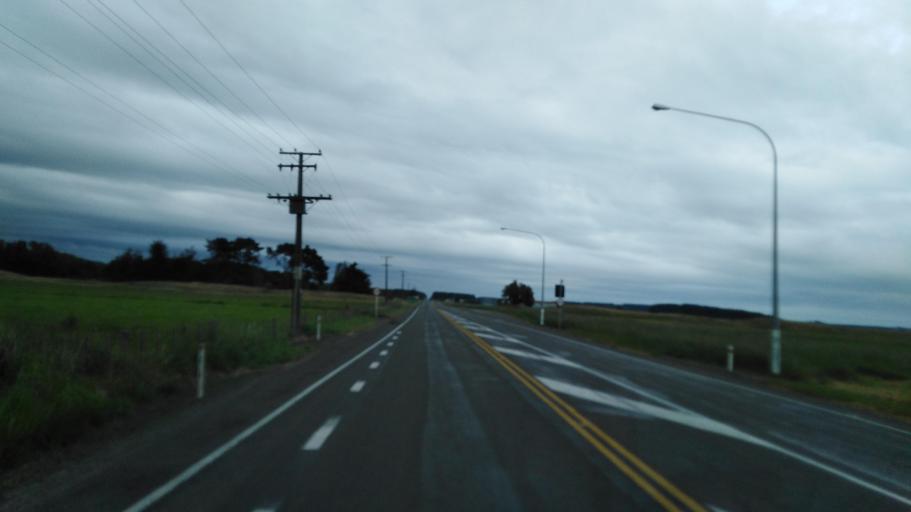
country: NZ
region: Manawatu-Wanganui
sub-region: Horowhenua District
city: Foxton
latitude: -40.3921
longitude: 175.3149
